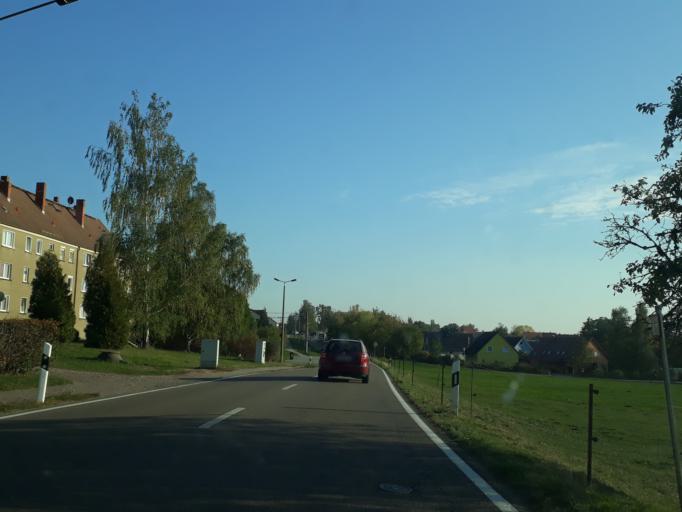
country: DE
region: Saxony
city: Wilsdruff
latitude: 51.0371
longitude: 13.5465
